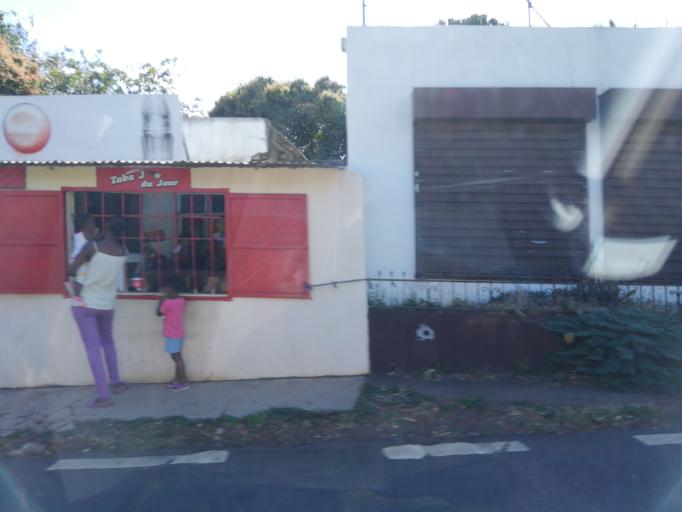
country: MU
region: Moka
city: Pailles
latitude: -20.1834
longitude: 57.4758
